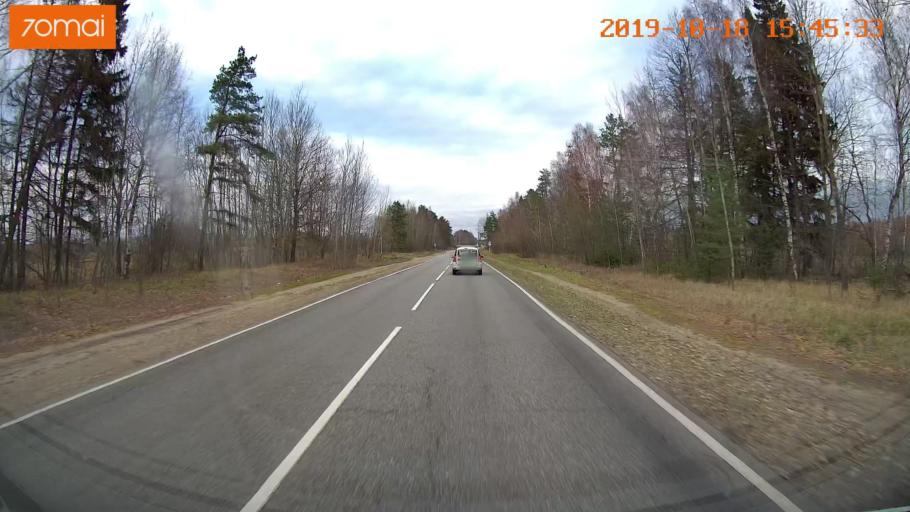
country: RU
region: Vladimir
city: Golovino
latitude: 55.9953
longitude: 40.5617
